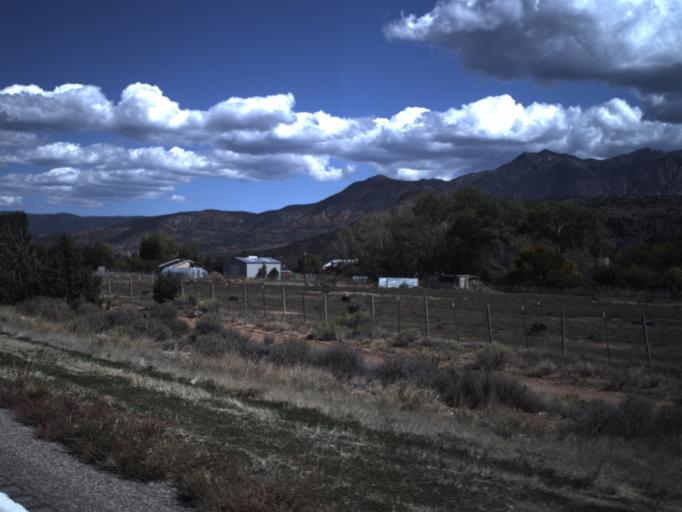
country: US
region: Utah
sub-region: Washington County
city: Ivins
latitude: 37.3635
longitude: -113.6687
